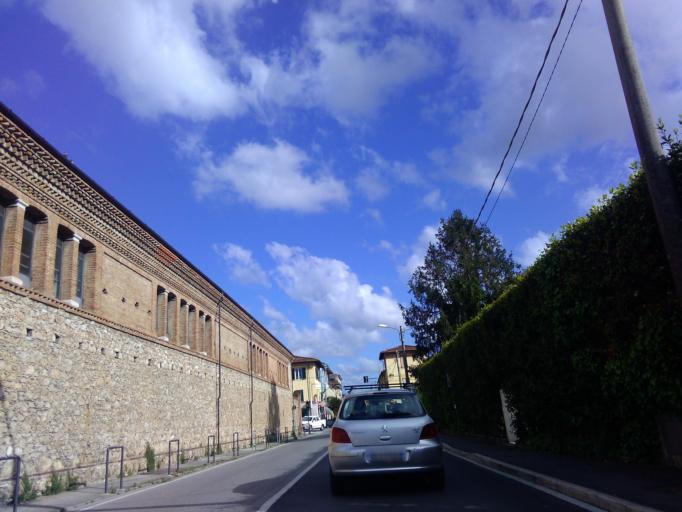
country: IT
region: Tuscany
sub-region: Provincia di Lucca
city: Pietrasanta
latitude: 43.9617
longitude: 10.2262
